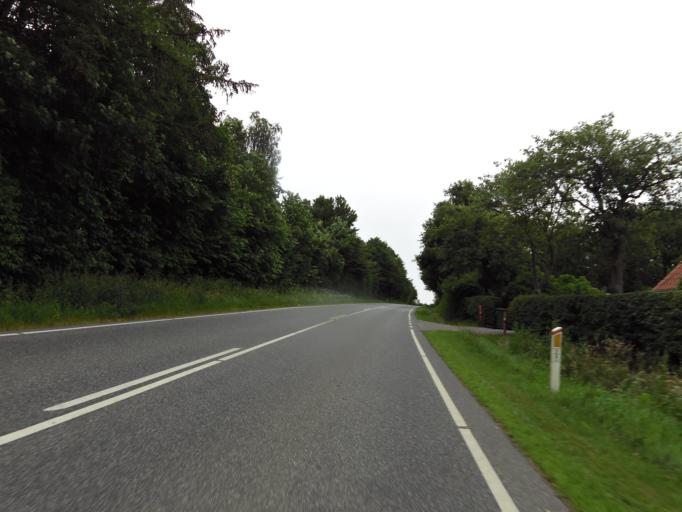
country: DK
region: South Denmark
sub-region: Tonder Kommune
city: Logumkloster
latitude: 55.1591
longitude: 8.9616
